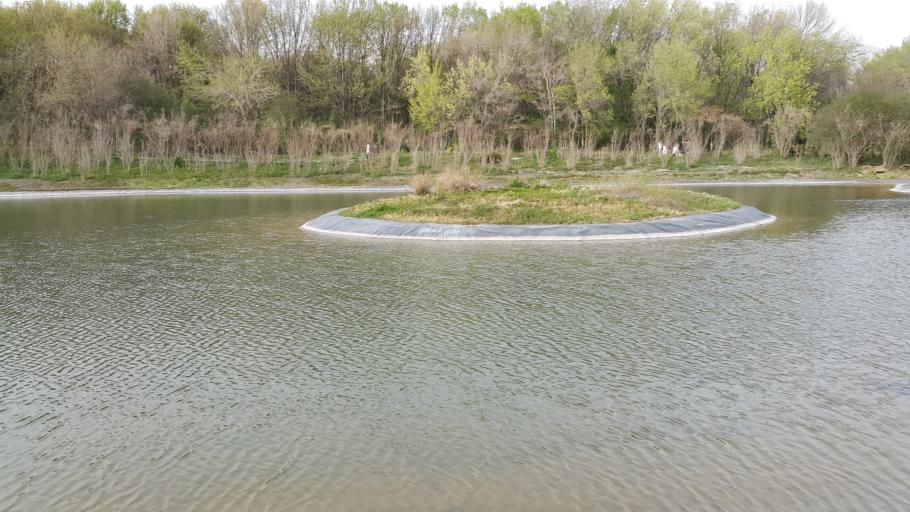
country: IR
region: Tehran
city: Shahr-e Qods
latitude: 35.7380
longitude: 51.1791
